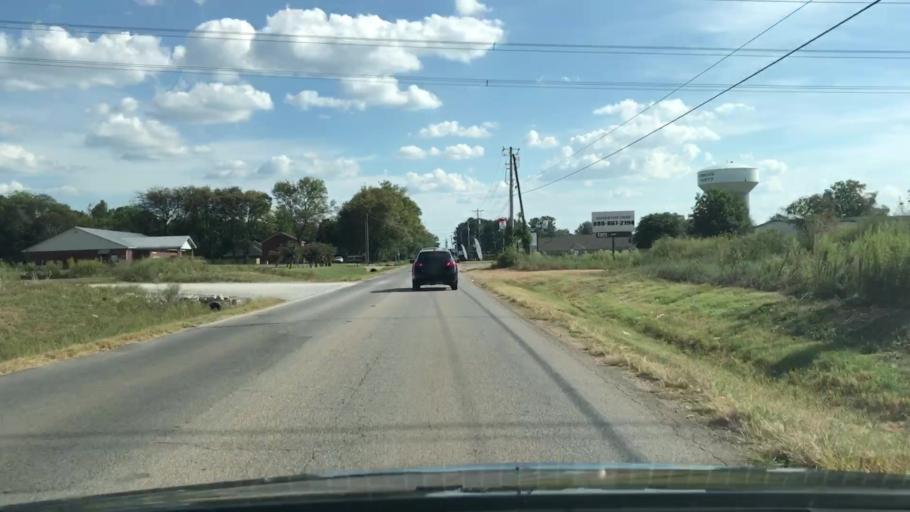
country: US
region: Alabama
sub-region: Madison County
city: Harvest
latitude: 34.8146
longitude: -86.7492
